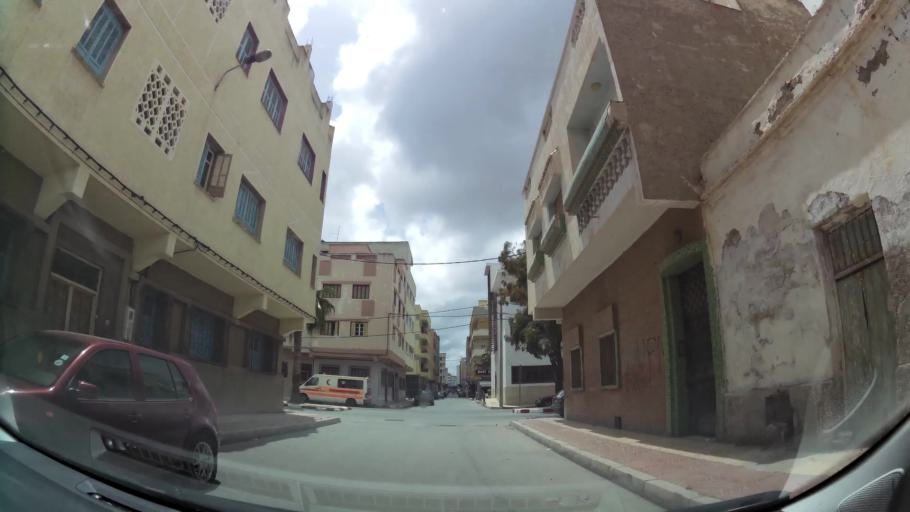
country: MA
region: Oriental
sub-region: Nador
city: Nador
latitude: 35.1799
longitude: -2.9227
